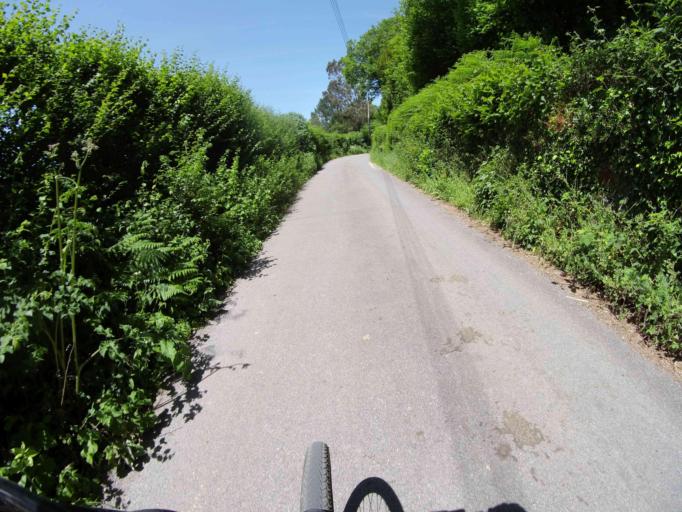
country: GB
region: England
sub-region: Devon
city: Bovey Tracey
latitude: 50.6141
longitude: -3.7120
